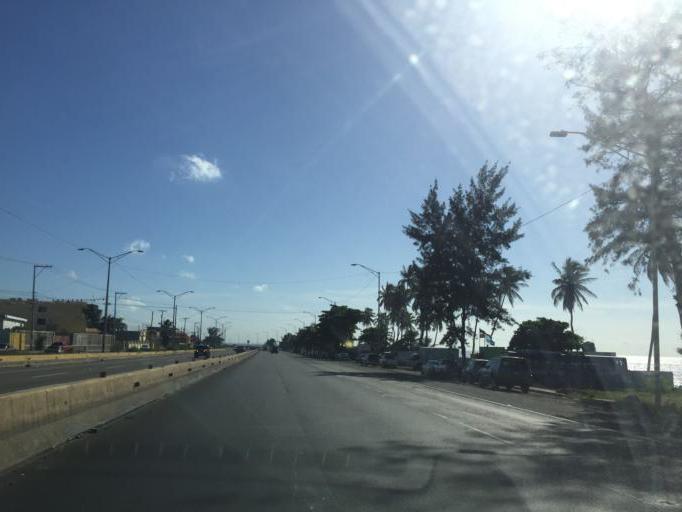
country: DO
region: Santo Domingo
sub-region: Santo Domingo
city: Santo Domingo Este
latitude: 18.4662
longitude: -69.8229
